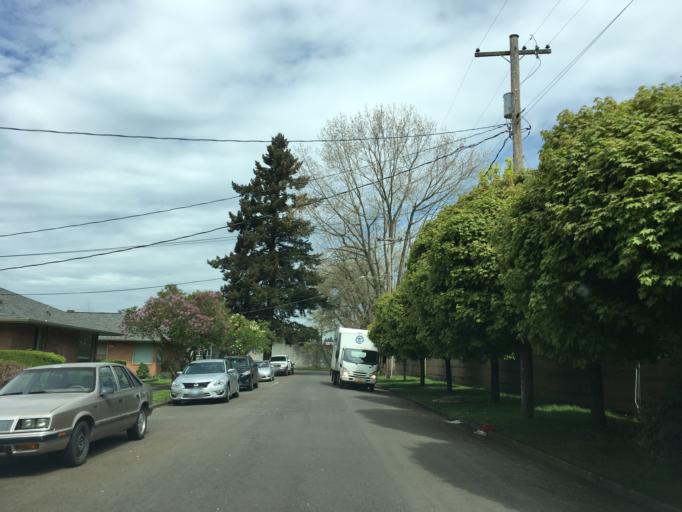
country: US
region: Oregon
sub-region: Multnomah County
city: Lents
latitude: 45.5306
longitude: -122.5964
